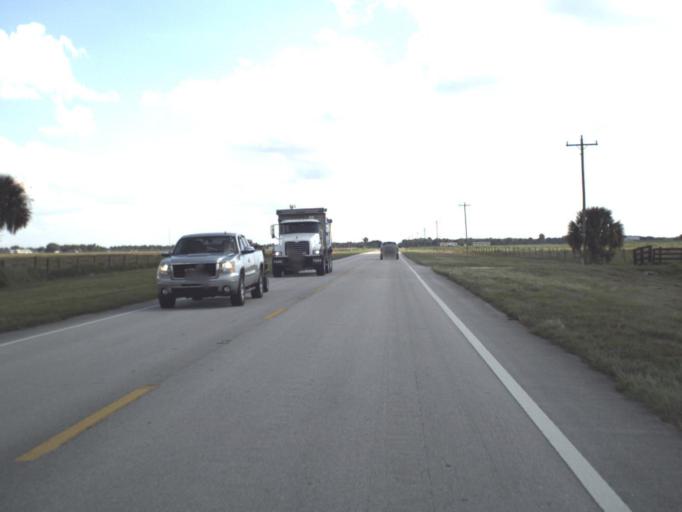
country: US
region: Florida
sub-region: Okeechobee County
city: Okeechobee
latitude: 27.3379
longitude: -80.9373
